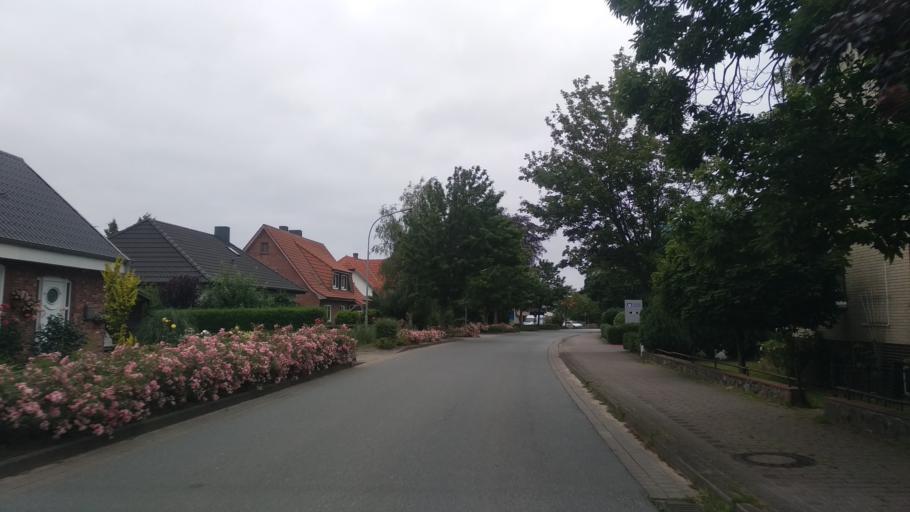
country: DE
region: Schleswig-Holstein
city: Langballig
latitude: 54.7984
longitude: 9.6368
